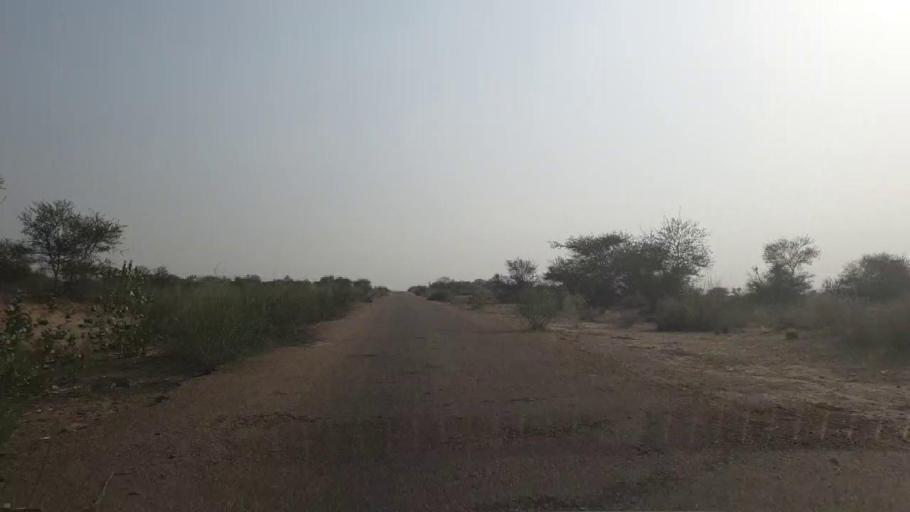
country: PK
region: Sindh
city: Chor
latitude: 25.4681
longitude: 69.9684
